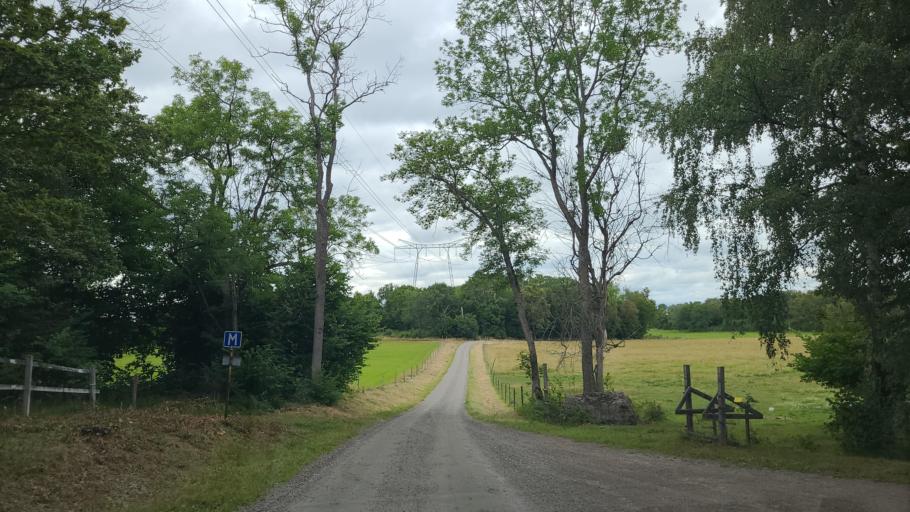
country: SE
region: Stockholm
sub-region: Upplands-Bro Kommun
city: Bro
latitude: 59.4568
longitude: 17.5817
